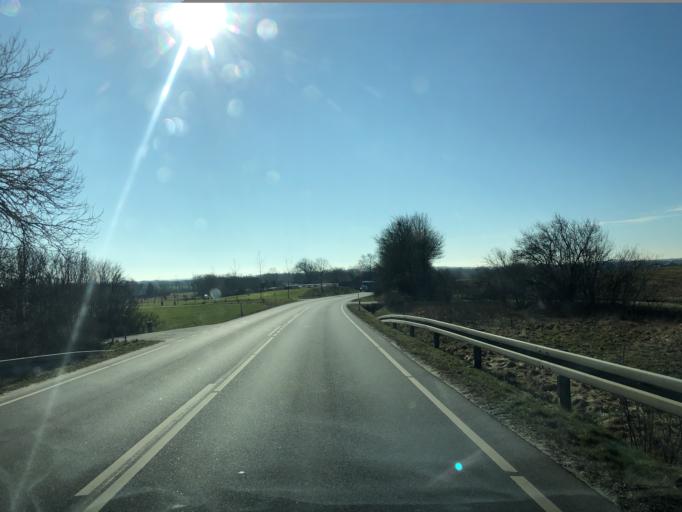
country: DK
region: Central Jutland
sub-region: Ikast-Brande Kommune
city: Bording Kirkeby
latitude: 56.1539
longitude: 9.2323
